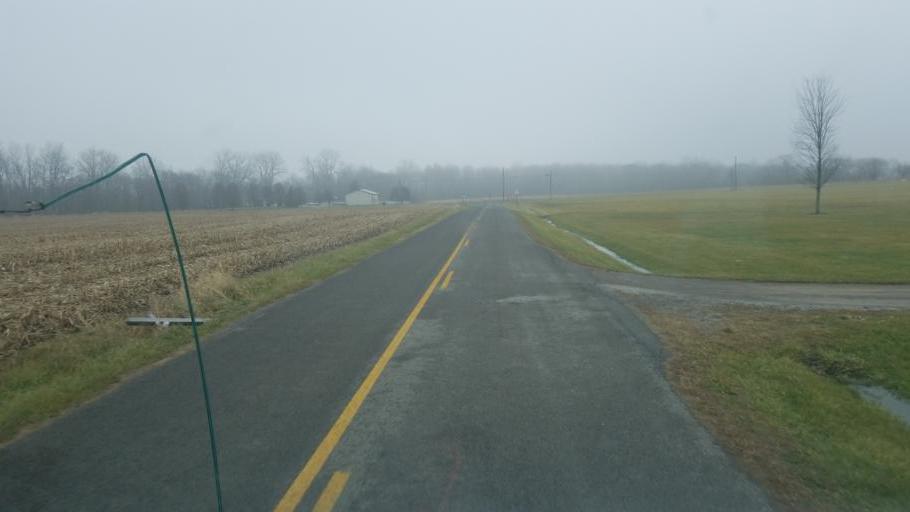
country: US
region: Ohio
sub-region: Hardin County
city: Kenton
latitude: 40.5033
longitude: -83.5226
